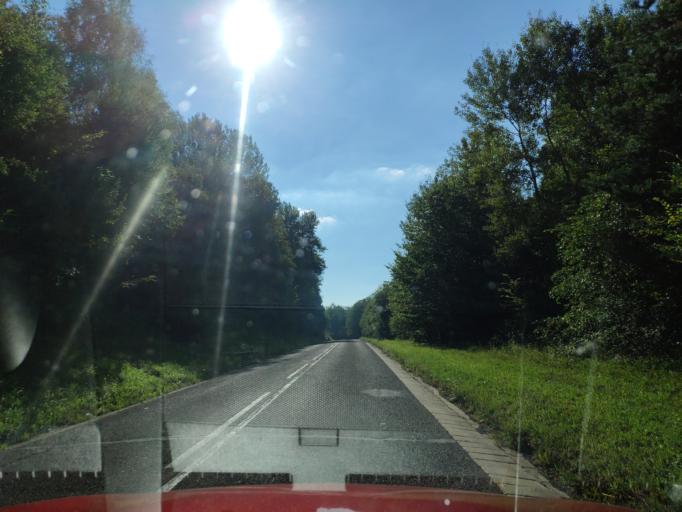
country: SK
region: Presovsky
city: Snina
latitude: 49.0450
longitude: 22.2751
